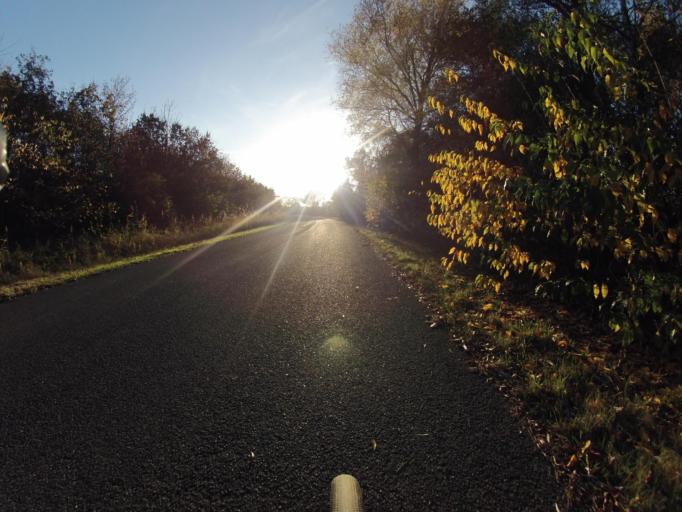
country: DE
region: North Rhine-Westphalia
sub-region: Regierungsbezirk Munster
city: Horstel
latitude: 52.2913
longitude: 7.6109
